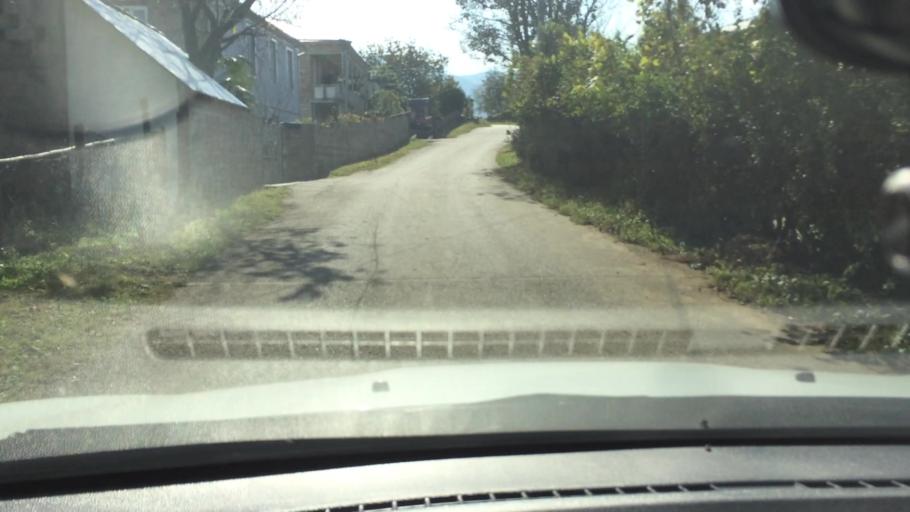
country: GE
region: Ajaria
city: Kobuleti
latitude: 41.8148
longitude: 41.8231
